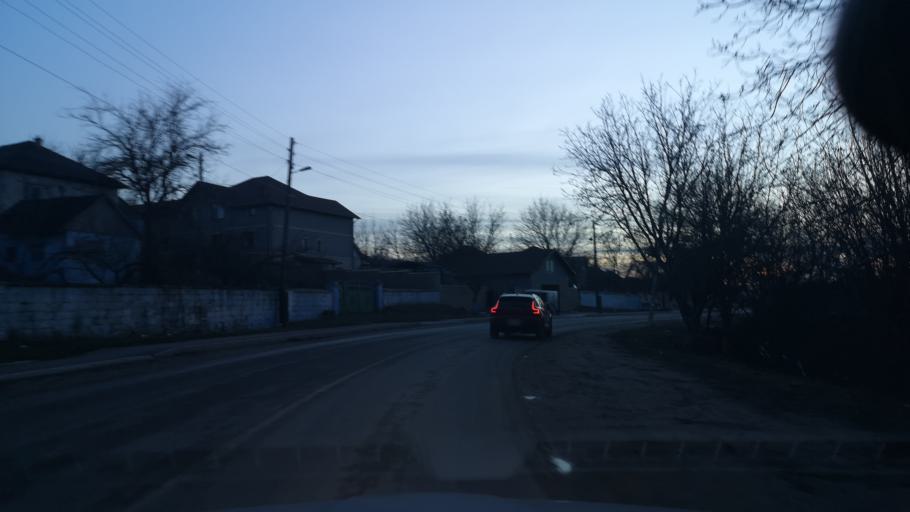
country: MD
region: Orhei
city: Orhei
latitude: 47.3067
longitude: 28.9296
